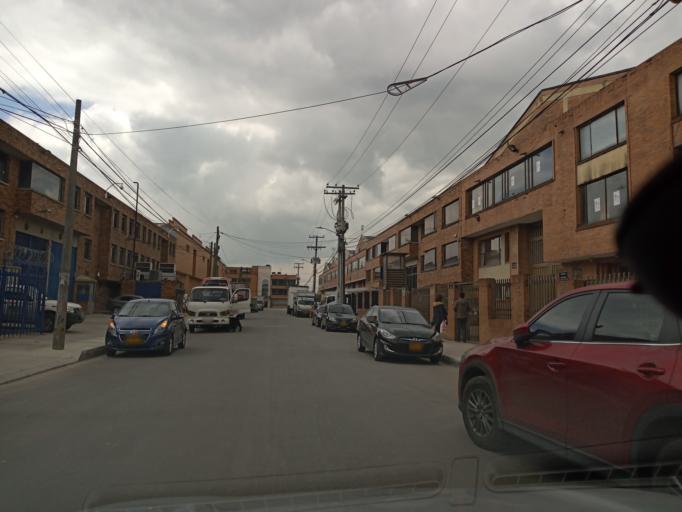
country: CO
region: Bogota D.C.
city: Bogota
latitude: 4.6512
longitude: -74.1191
